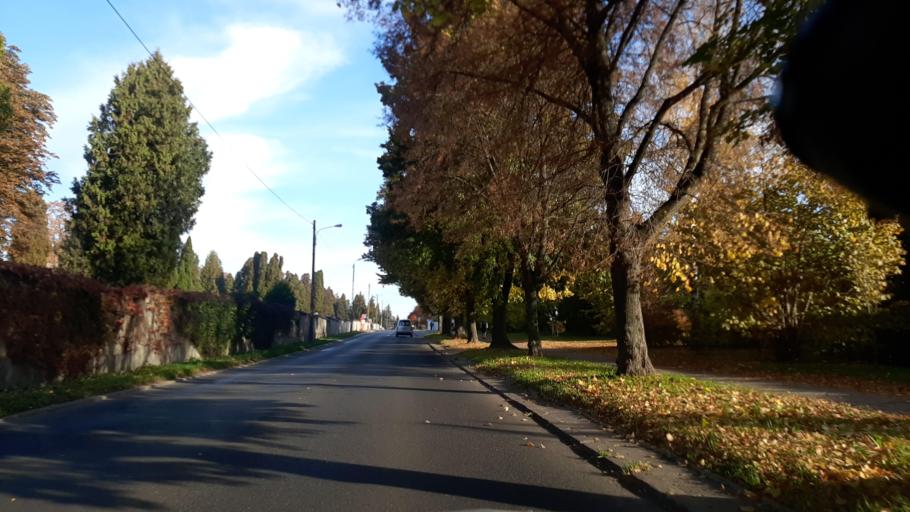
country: PL
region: Lublin Voivodeship
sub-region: Powiat lubelski
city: Lublin
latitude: 51.2622
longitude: 22.5805
